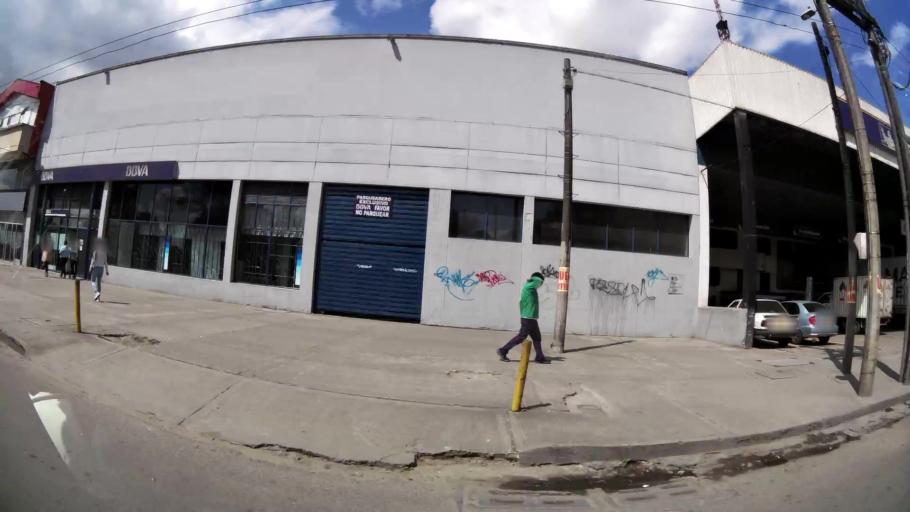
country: CO
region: Bogota D.C.
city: Bogota
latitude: 4.6343
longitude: -74.1137
